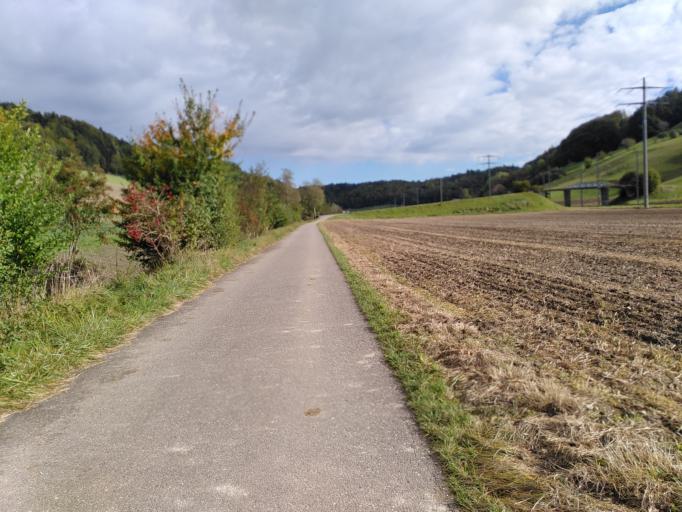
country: CH
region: Bern
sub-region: Oberaargau
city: Seeberg
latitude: 47.1335
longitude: 7.6821
